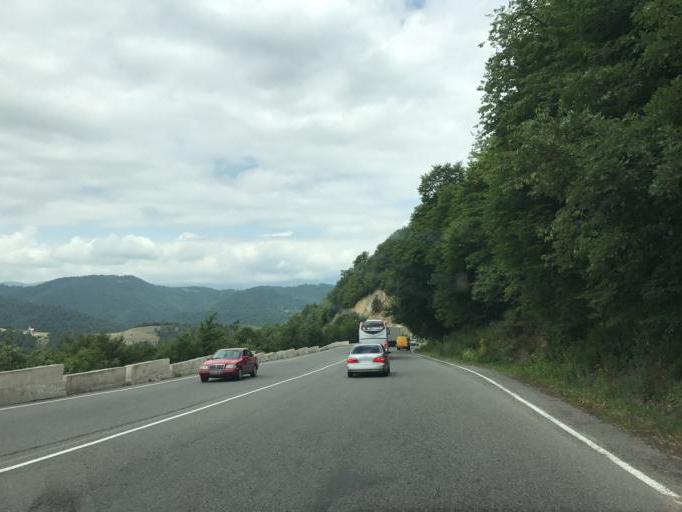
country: AM
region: Tavush
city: Dilijan
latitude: 40.6916
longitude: 44.8595
